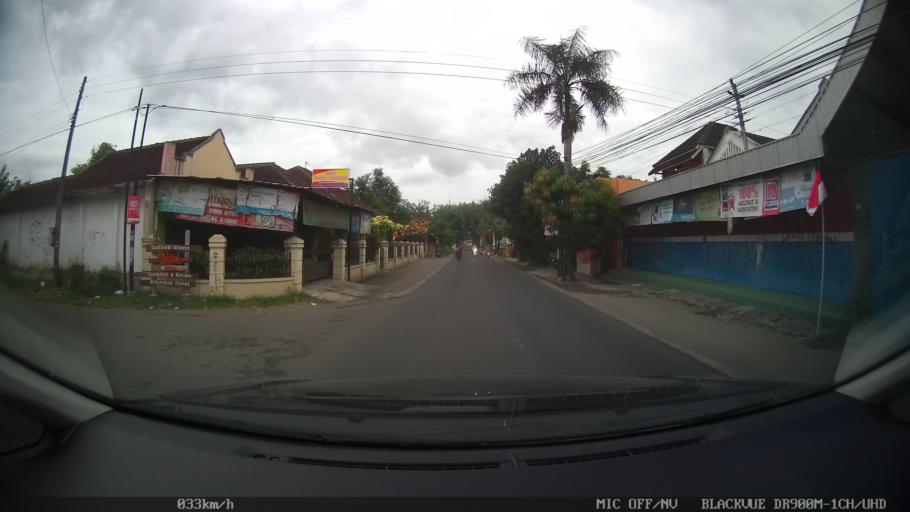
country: ID
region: Daerah Istimewa Yogyakarta
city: Sewon
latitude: -7.8631
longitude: 110.4084
